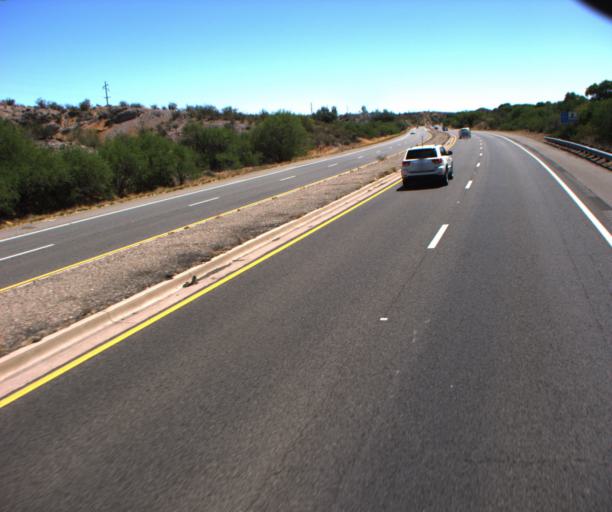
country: US
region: Arizona
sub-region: Maricopa County
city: Wickenburg
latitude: 33.9119
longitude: -112.6761
